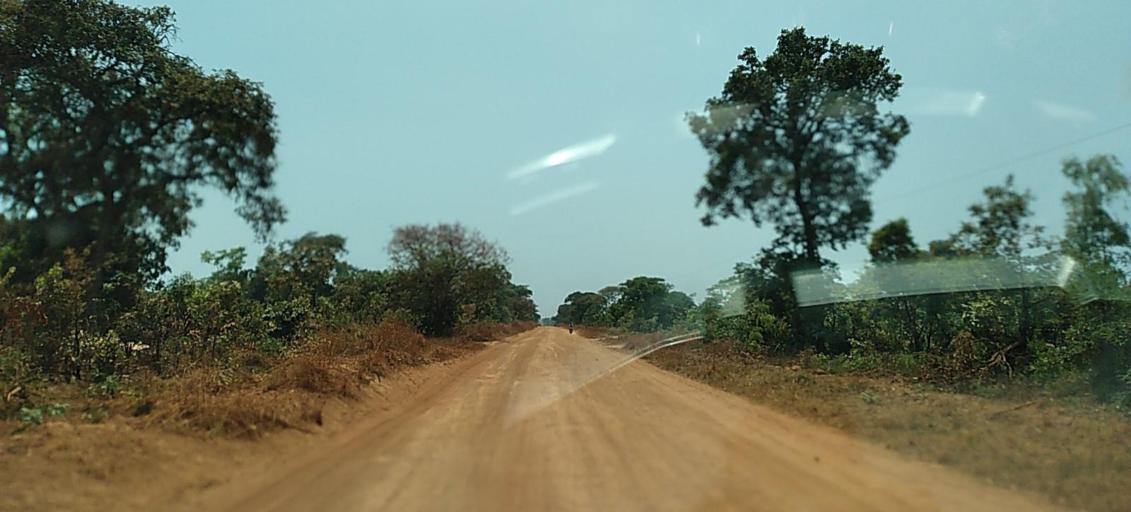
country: CD
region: Katanga
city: Kipushi
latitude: -11.9297
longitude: 26.9867
